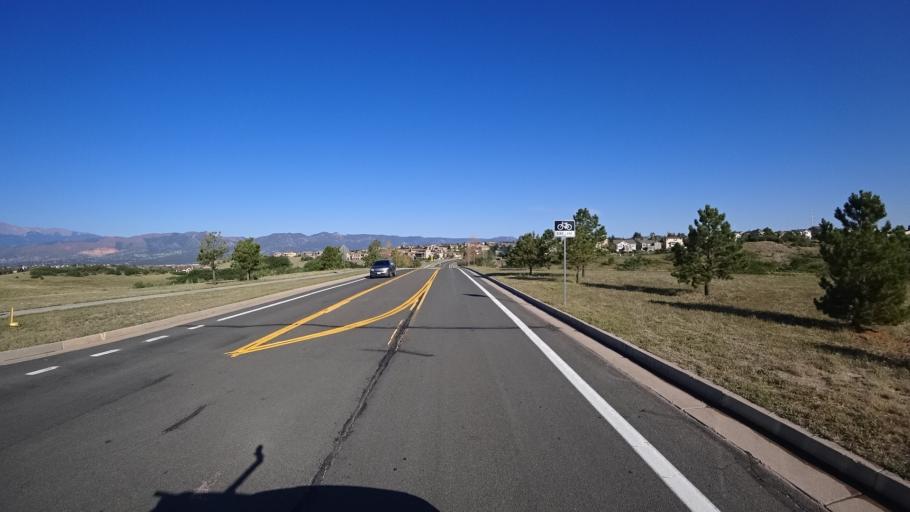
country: US
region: Colorado
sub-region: El Paso County
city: Black Forest
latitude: 38.9727
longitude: -104.7546
